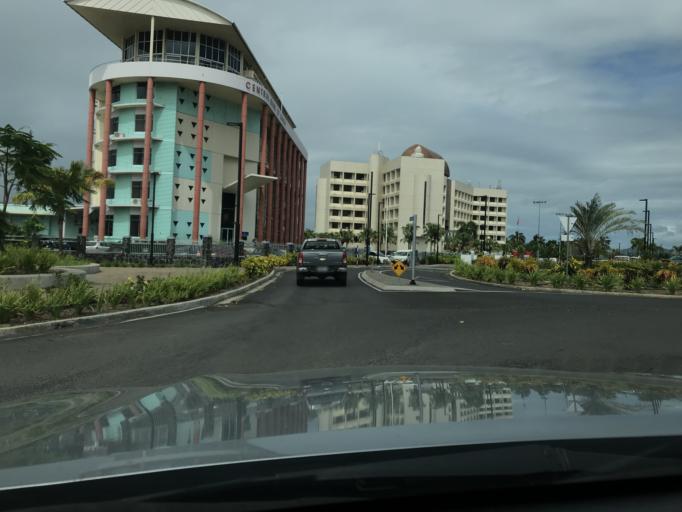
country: WS
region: Tuamasaga
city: Apia
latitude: -13.8302
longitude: -171.7685
